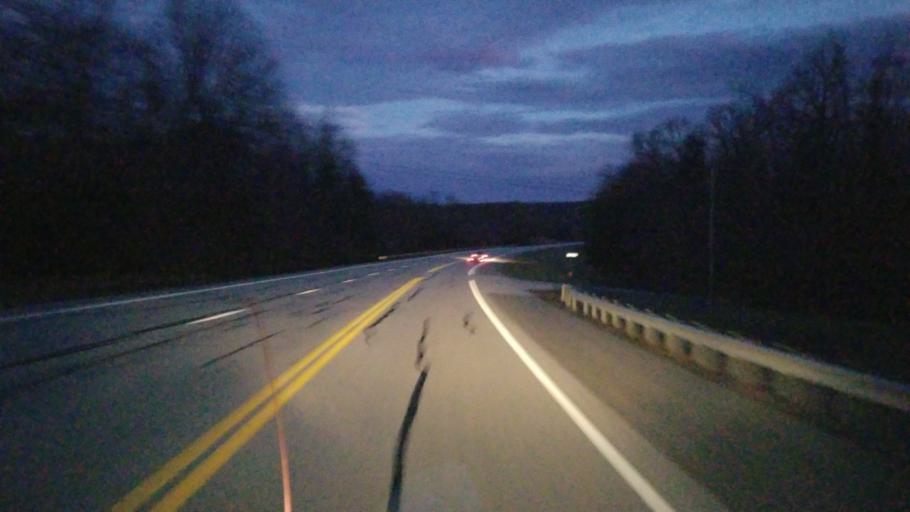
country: US
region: Tennessee
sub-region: Sequatchie County
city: Dunlap
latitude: 35.4908
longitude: -85.4709
